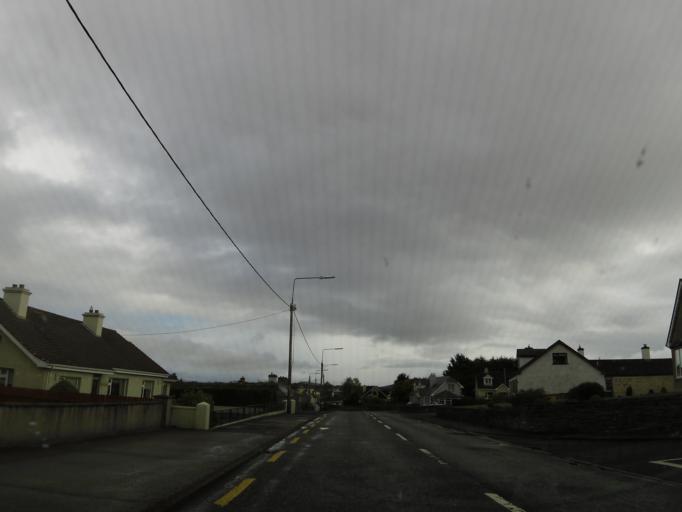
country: IE
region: Connaught
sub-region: Sligo
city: Tobercurry
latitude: 54.0493
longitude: -8.7356
